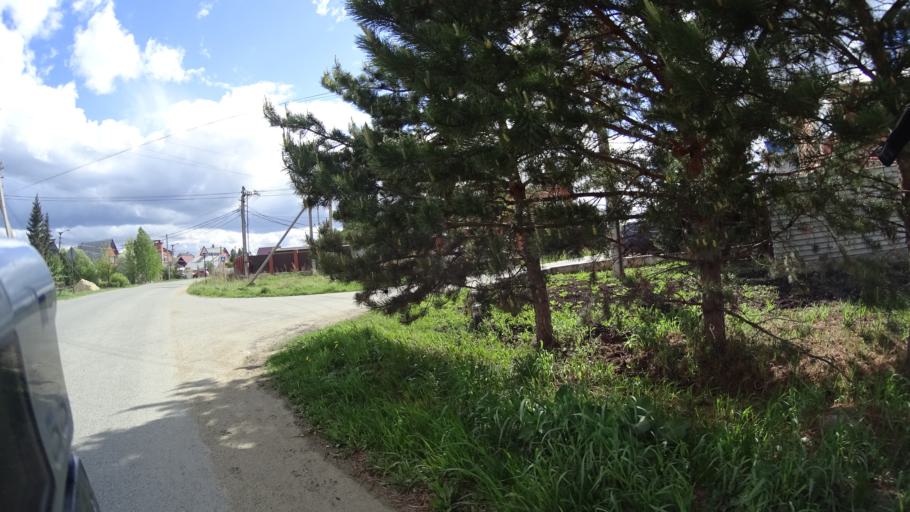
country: RU
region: Chelyabinsk
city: Sargazy
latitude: 55.1483
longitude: 61.2375
